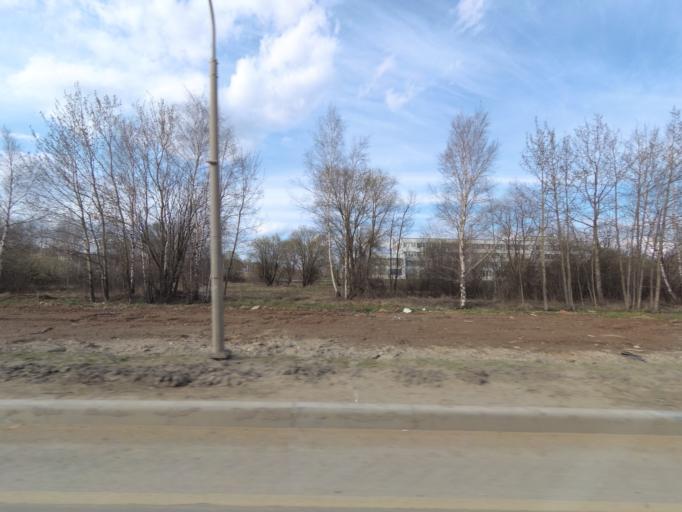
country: RU
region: Moskovskaya
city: Sheremet'yevskiy
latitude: 55.9792
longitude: 37.4538
